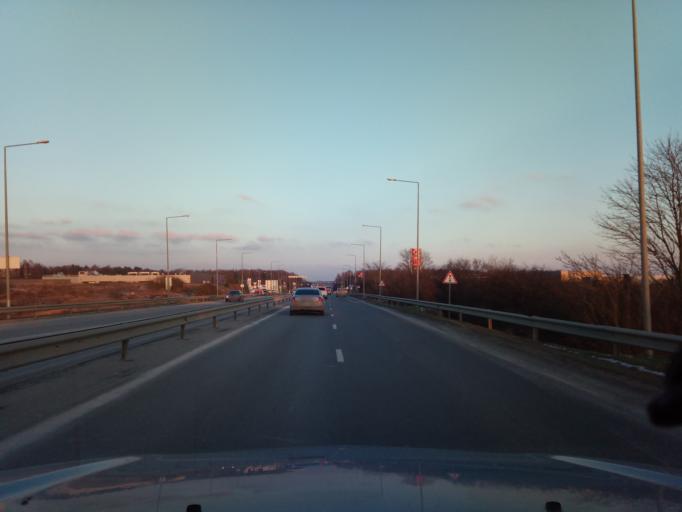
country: LT
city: Lentvaris
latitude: 54.6228
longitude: 25.1070
